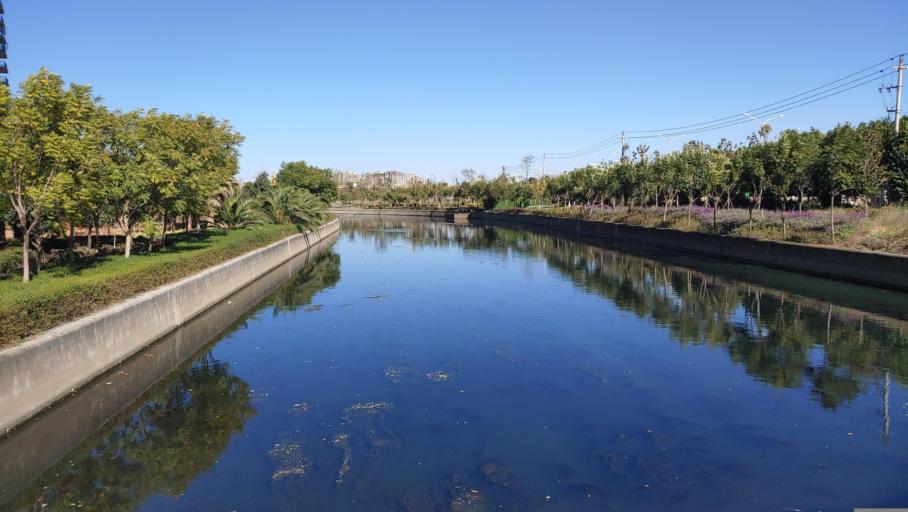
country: CN
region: Yunnan
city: Liujia
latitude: 24.9611
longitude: 102.7026
